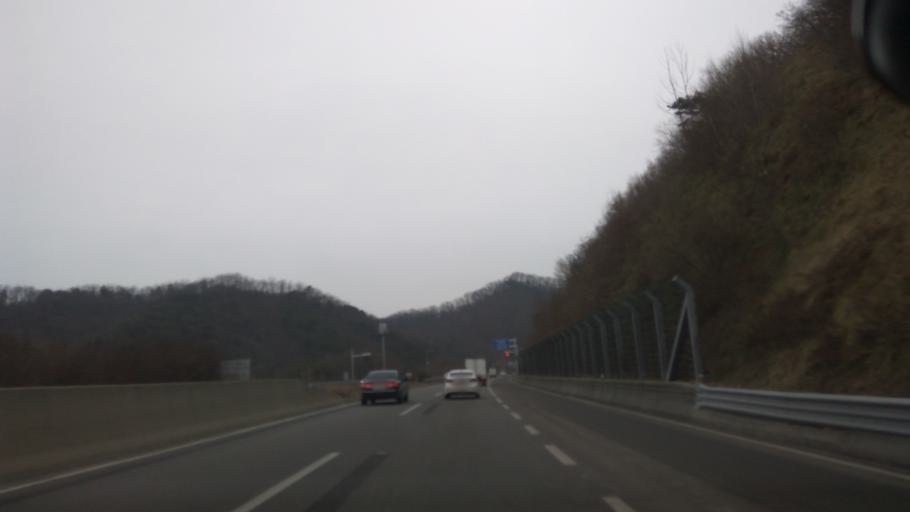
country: KR
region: Gangwon-do
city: Sindong
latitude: 37.7386
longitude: 127.6348
